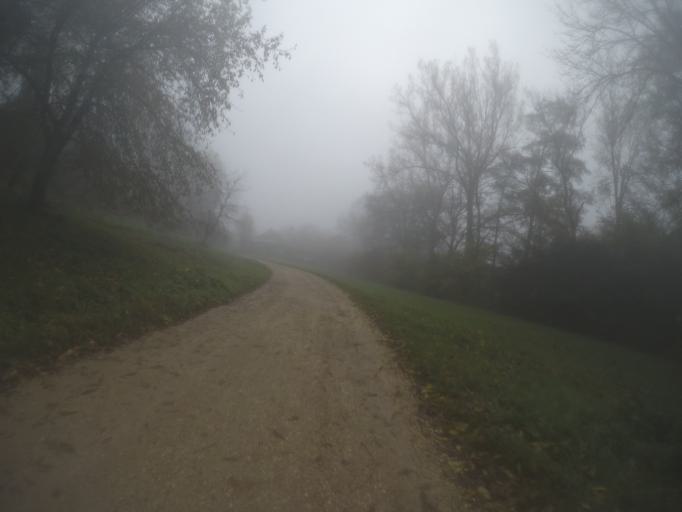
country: DE
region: Baden-Wuerttemberg
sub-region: Regierungsbezirk Stuttgart
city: Neuhausen auf den Fildern
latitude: 48.7042
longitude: 9.2849
